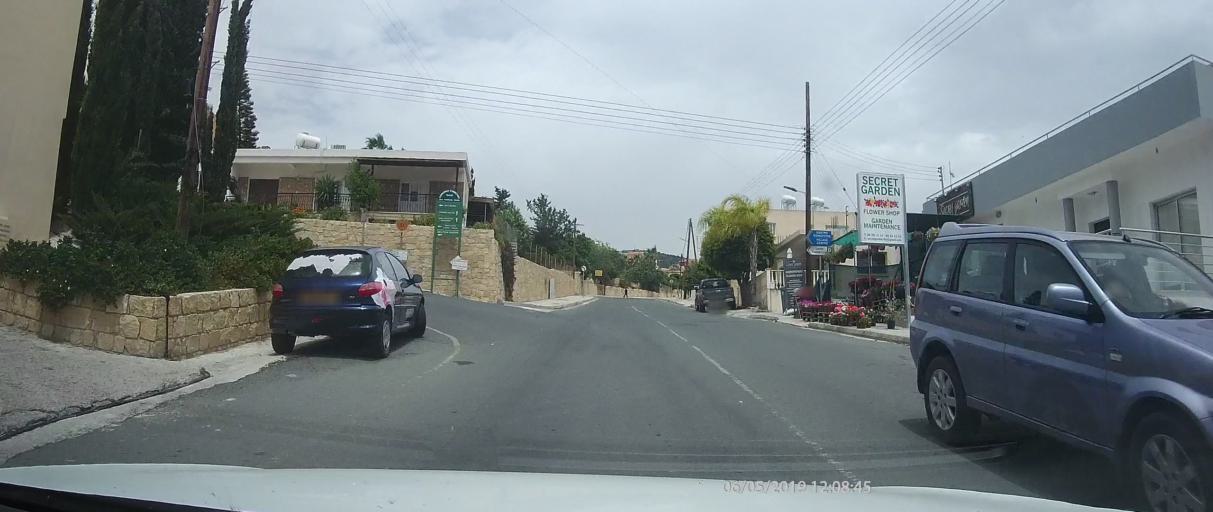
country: CY
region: Pafos
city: Tala
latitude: 34.8358
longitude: 32.4318
